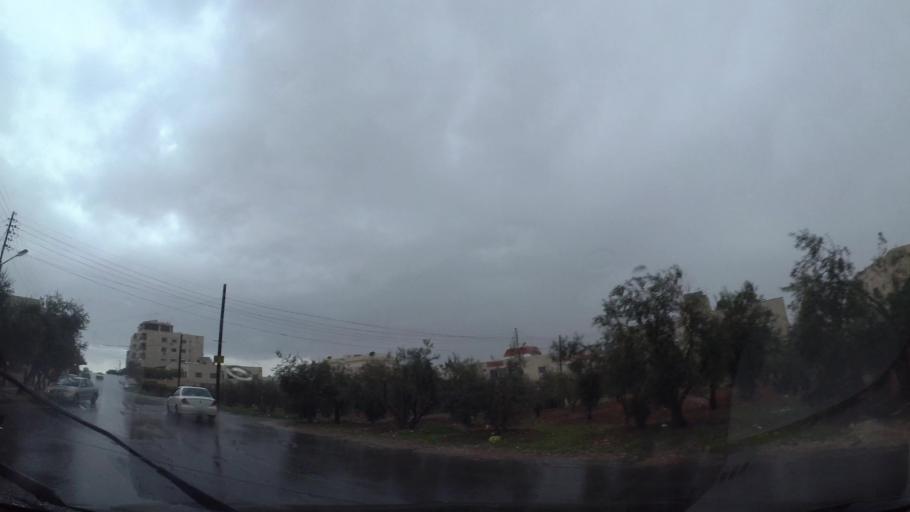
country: JO
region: Amman
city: Amman
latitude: 32.0015
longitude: 35.9556
